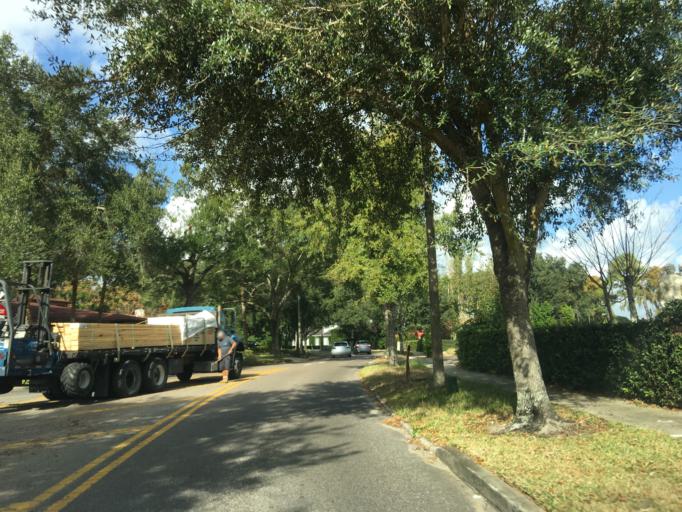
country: US
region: Florida
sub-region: Orange County
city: Winter Park
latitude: 28.6075
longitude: -81.3493
